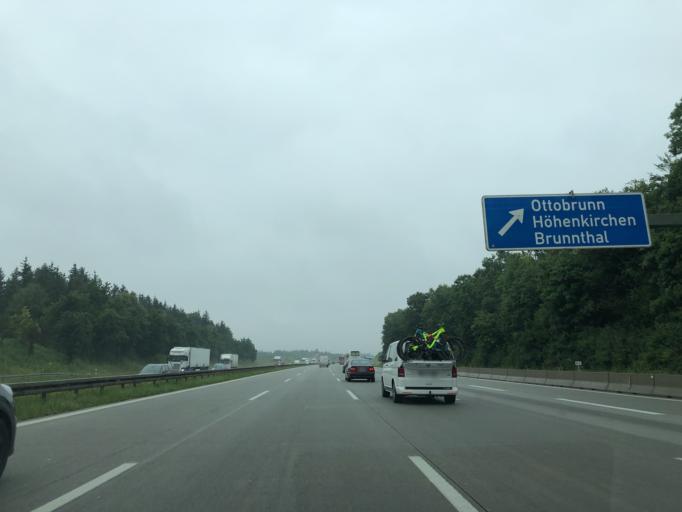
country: DE
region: Bavaria
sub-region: Upper Bavaria
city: Hohenbrunn
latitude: 48.0446
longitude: 11.6844
